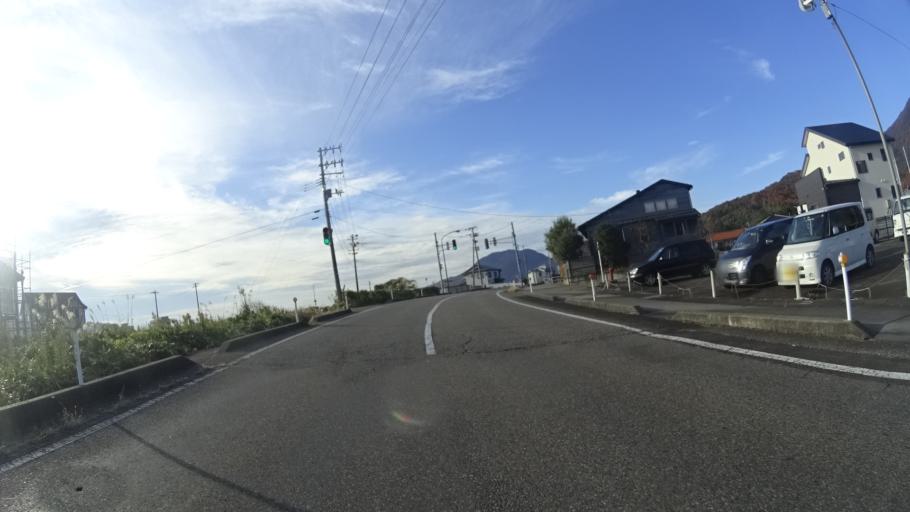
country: JP
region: Niigata
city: Yoshida-kasugacho
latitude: 37.6986
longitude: 138.8352
